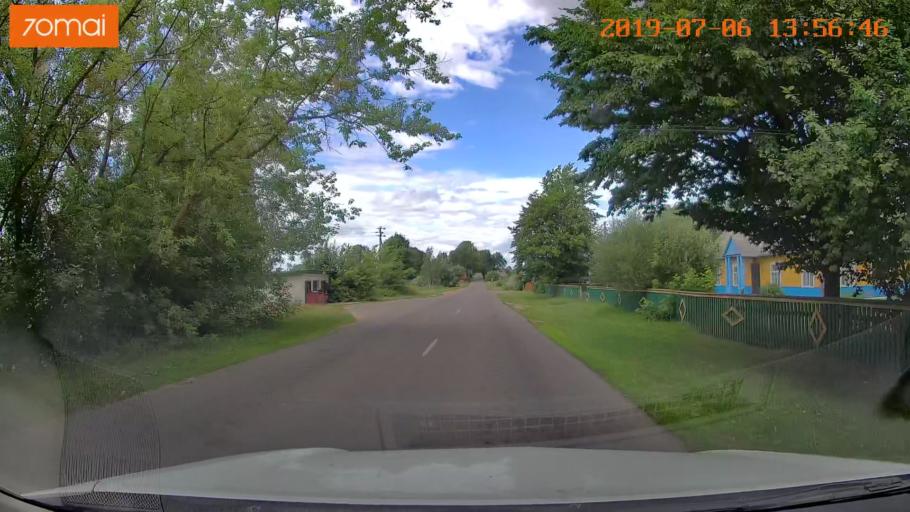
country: BY
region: Minsk
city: Ivyanyets
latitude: 53.7682
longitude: 26.8048
